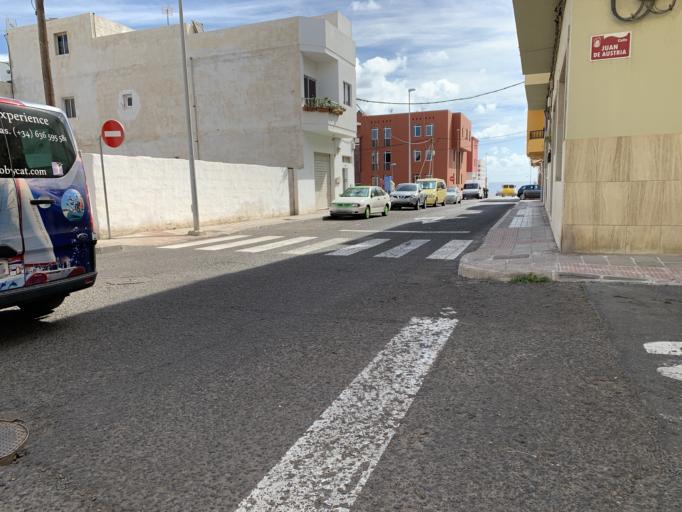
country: ES
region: Canary Islands
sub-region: Provincia de Las Palmas
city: Puerto del Rosario
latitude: 28.5030
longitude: -13.8489
